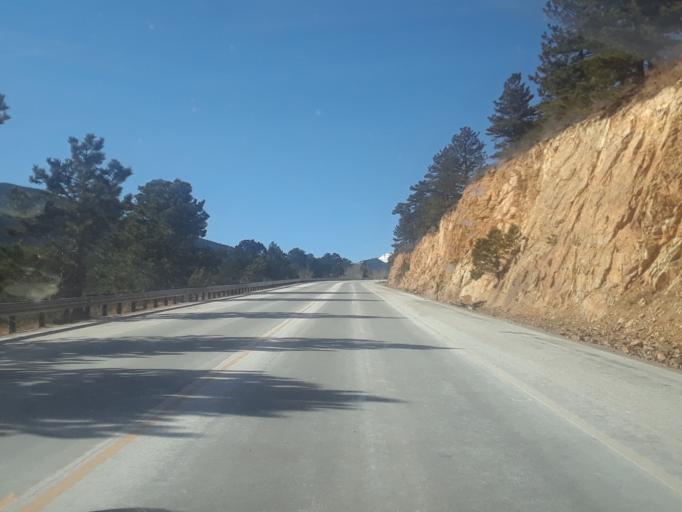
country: US
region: Colorado
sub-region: Larimer County
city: Estes Park
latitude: 40.1941
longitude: -105.5192
